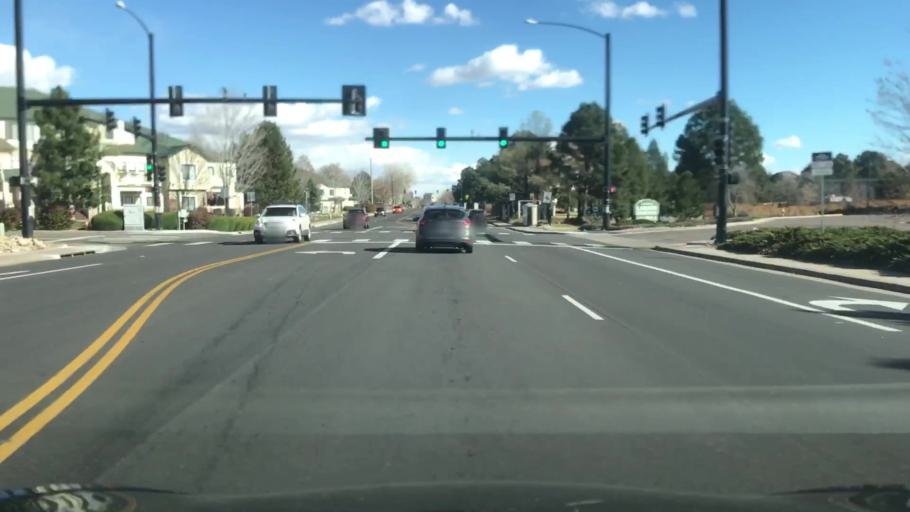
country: US
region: Colorado
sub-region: Arapahoe County
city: Glendale
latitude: 39.6893
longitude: -104.8887
